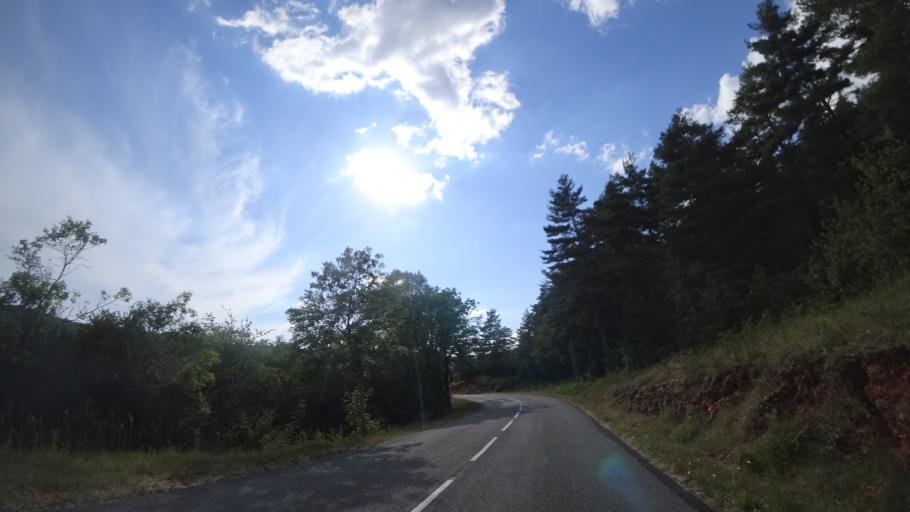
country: FR
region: Languedoc-Roussillon
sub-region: Departement de la Lozere
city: Chanac
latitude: 44.3835
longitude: 3.3160
